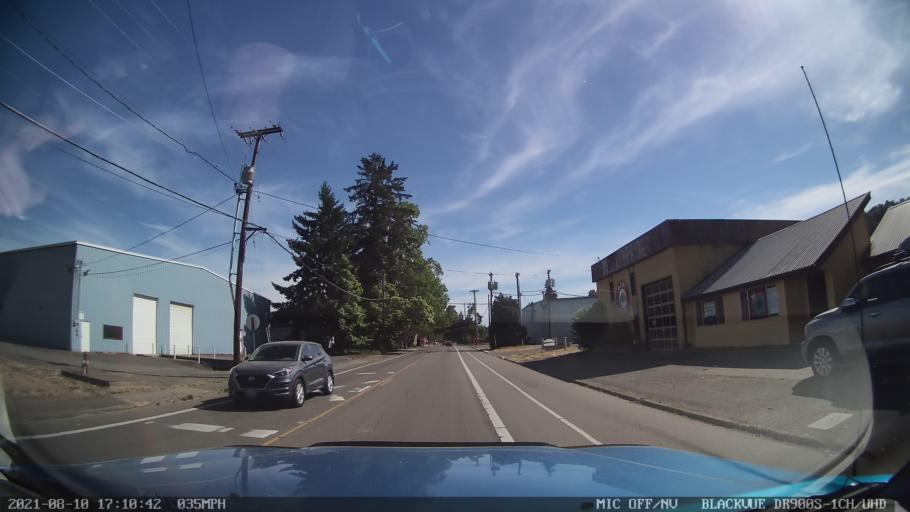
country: US
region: Oregon
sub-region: Marion County
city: Keizer
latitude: 44.9655
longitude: -123.0195
